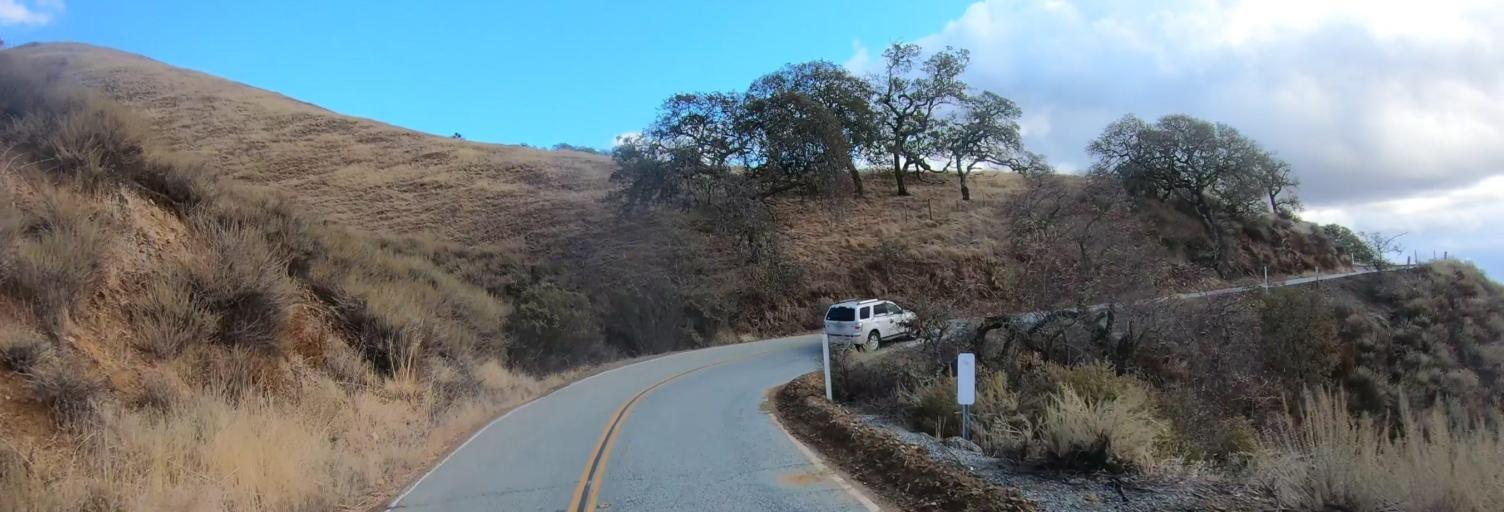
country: US
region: California
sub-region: Santa Clara County
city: East Foothills
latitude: 37.3321
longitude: -121.6966
